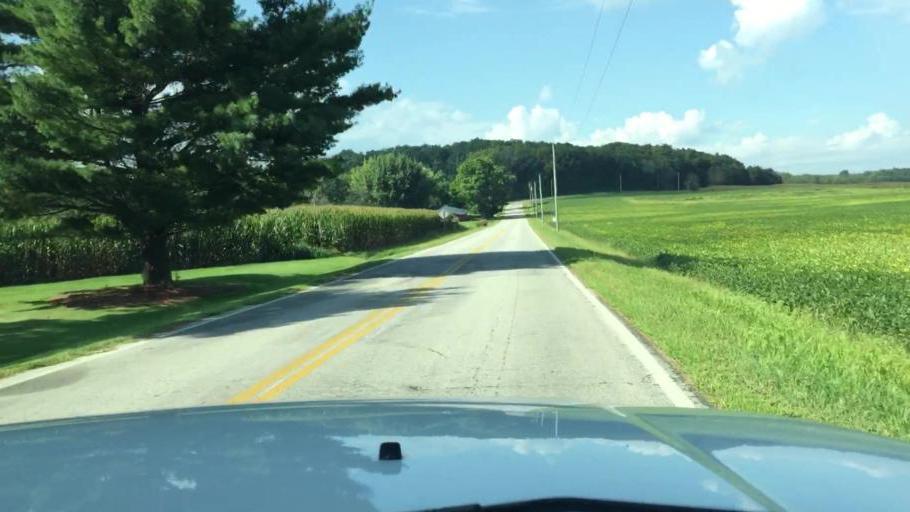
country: US
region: Ohio
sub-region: Clark County
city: Northridge
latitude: 39.9911
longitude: -83.6614
